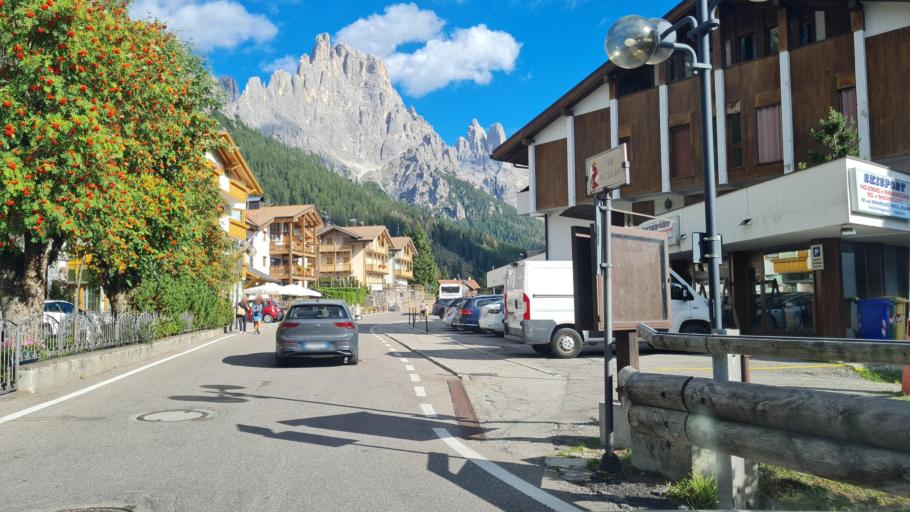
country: IT
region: Trentino-Alto Adige
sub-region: Provincia di Trento
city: Siror
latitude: 46.2628
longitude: 11.8036
